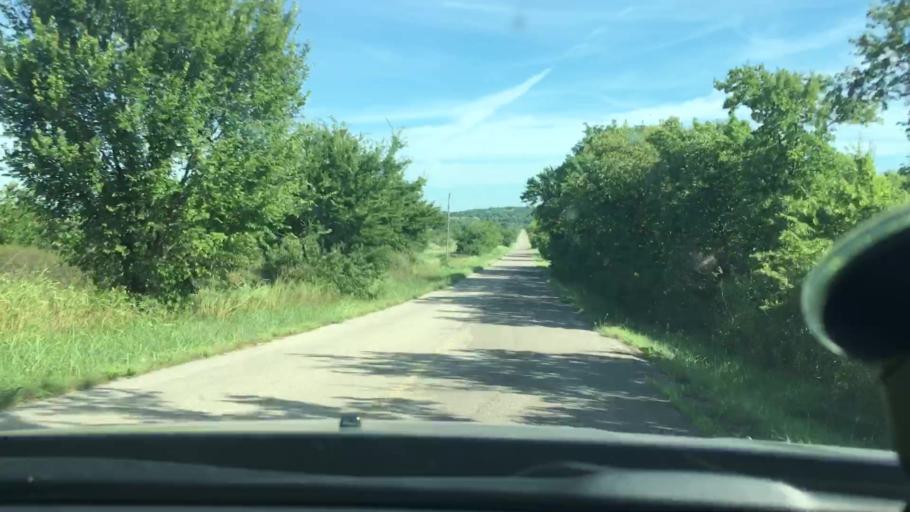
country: US
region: Oklahoma
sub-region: Carter County
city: Lone Grove
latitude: 34.3240
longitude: -97.2824
